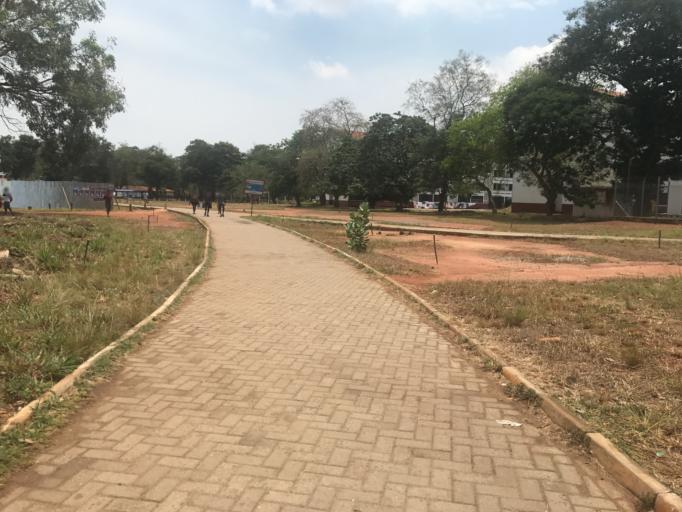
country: GH
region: Greater Accra
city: Medina Estates
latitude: 5.6452
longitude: -0.1860
